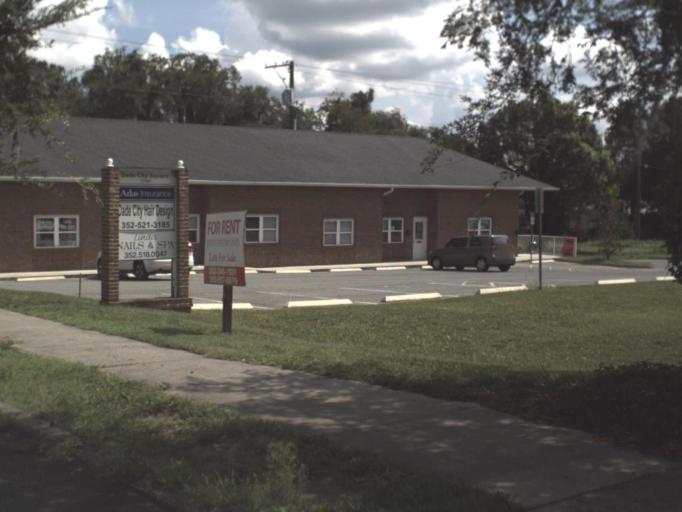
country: US
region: Florida
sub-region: Pasco County
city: Dade City
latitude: 28.3610
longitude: -82.1891
